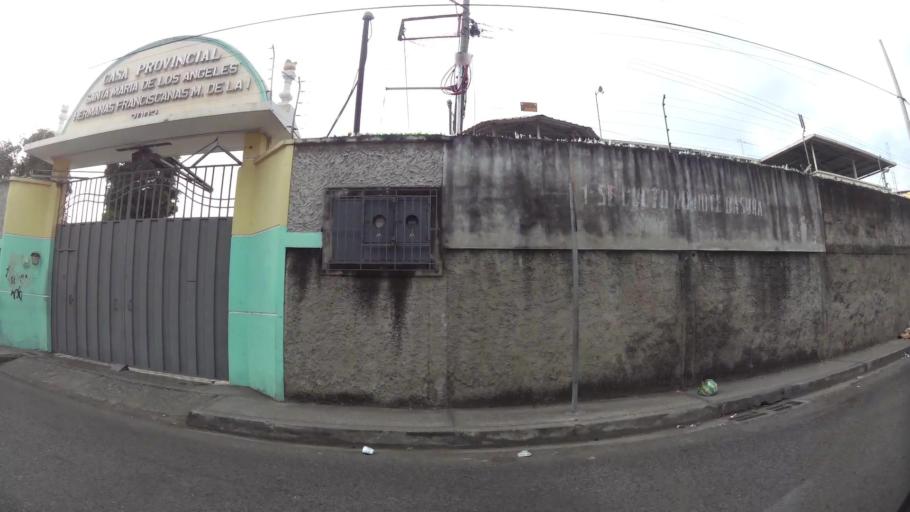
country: EC
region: Guayas
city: Guayaquil
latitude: -2.2491
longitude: -79.8960
